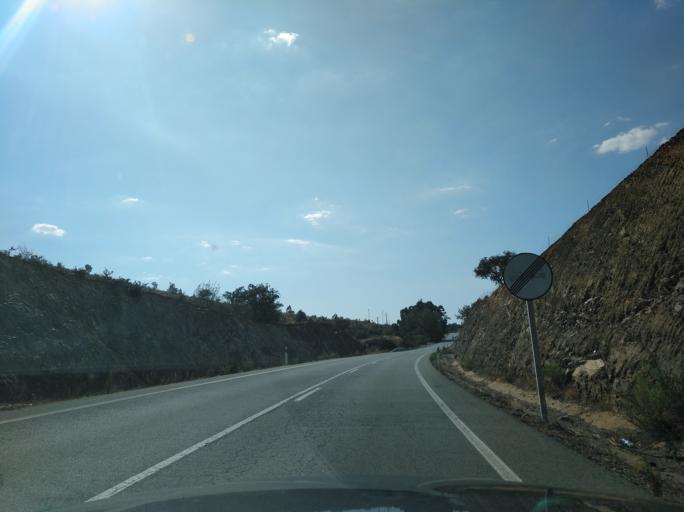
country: ES
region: Andalusia
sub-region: Provincia de Huelva
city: Santa Barbara de Casa
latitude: 37.7895
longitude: -7.1756
